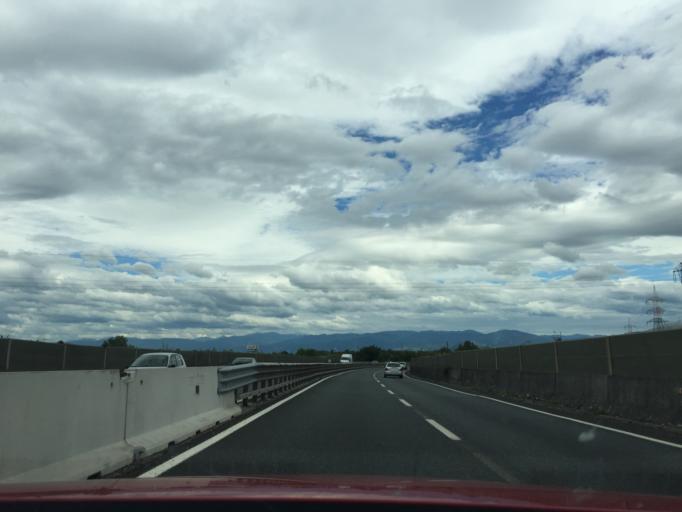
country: IT
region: Tuscany
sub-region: Province of Florence
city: Lastra a Signa
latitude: 43.7636
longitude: 11.1265
